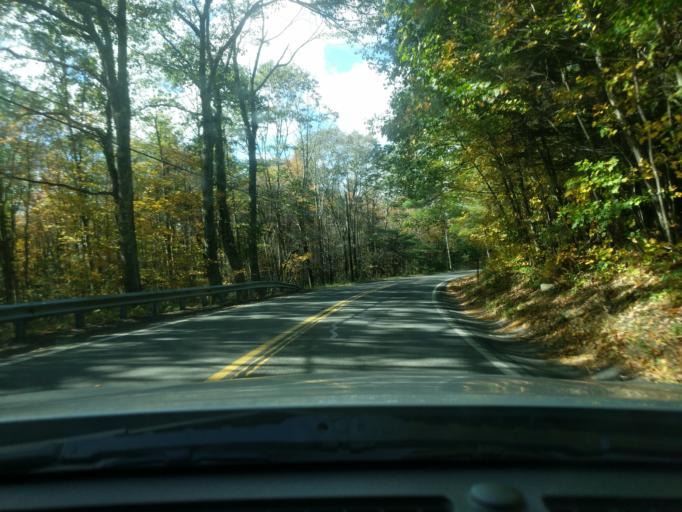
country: US
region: Massachusetts
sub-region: Berkshire County
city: Otis
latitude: 42.1703
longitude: -73.0148
